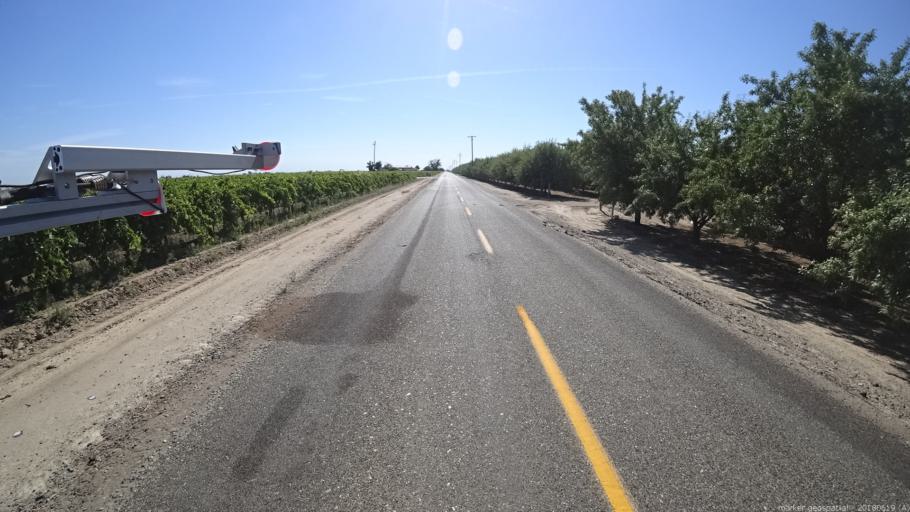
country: US
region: California
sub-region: Fresno County
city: Biola
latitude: 36.8368
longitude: -120.0383
